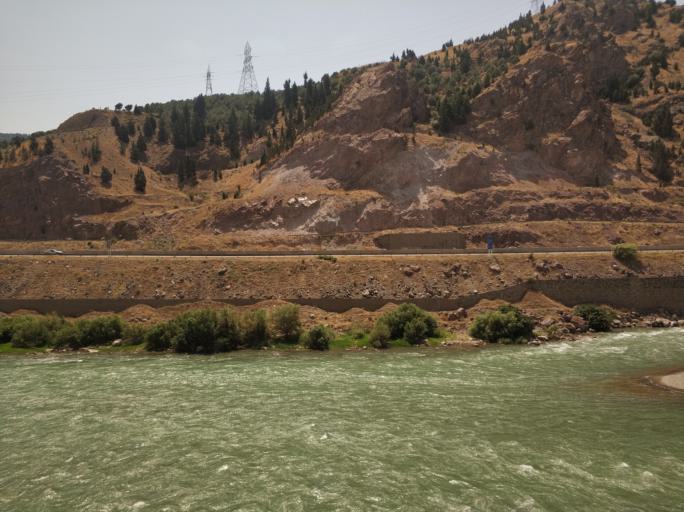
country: IR
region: Gilan
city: Pa'in-e Bazar-e Rudbar
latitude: 36.8373
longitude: 49.4509
